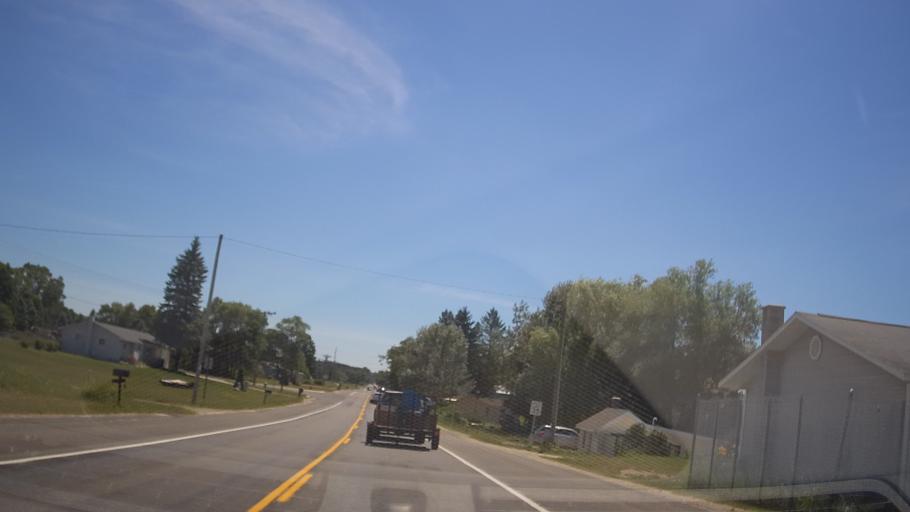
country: US
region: Michigan
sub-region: Grand Traverse County
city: Traverse City
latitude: 44.6601
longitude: -85.6966
